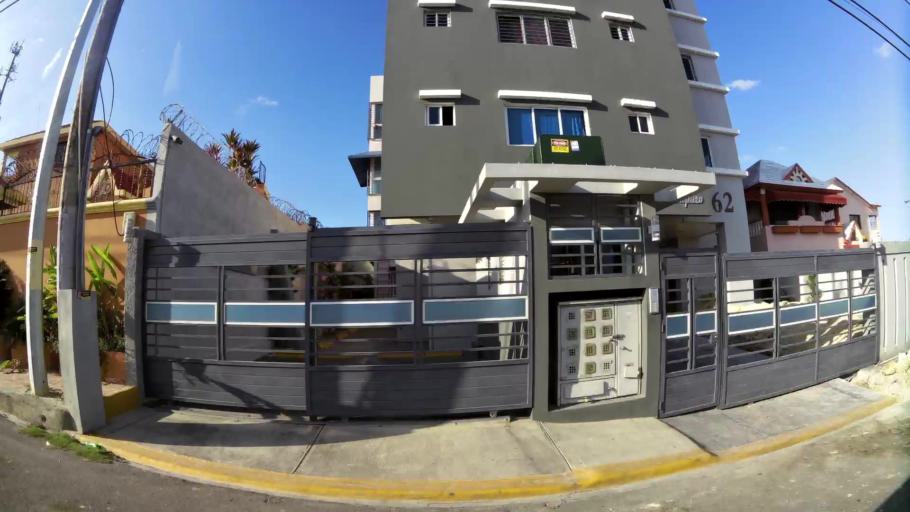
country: DO
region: Nacional
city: Ensanche Luperon
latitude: 18.5483
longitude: -69.9072
